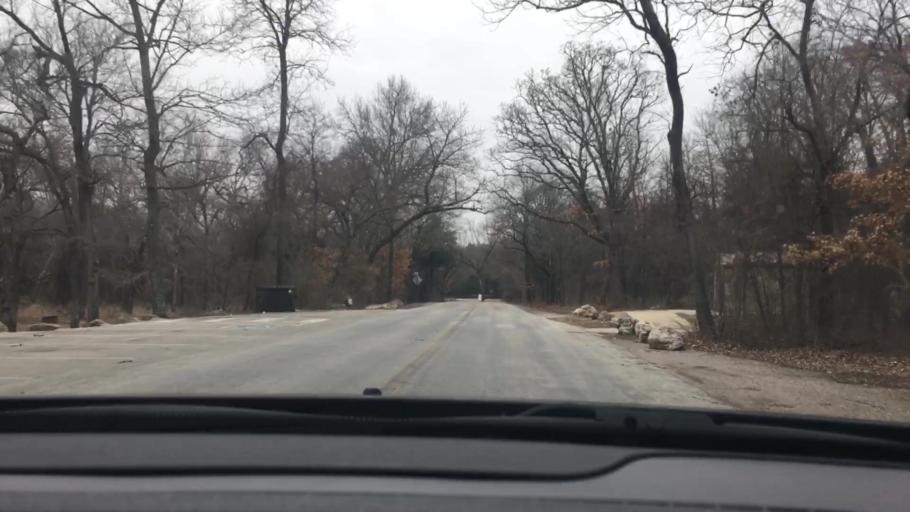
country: US
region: Oklahoma
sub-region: Murray County
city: Sulphur
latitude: 34.5021
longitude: -96.9651
